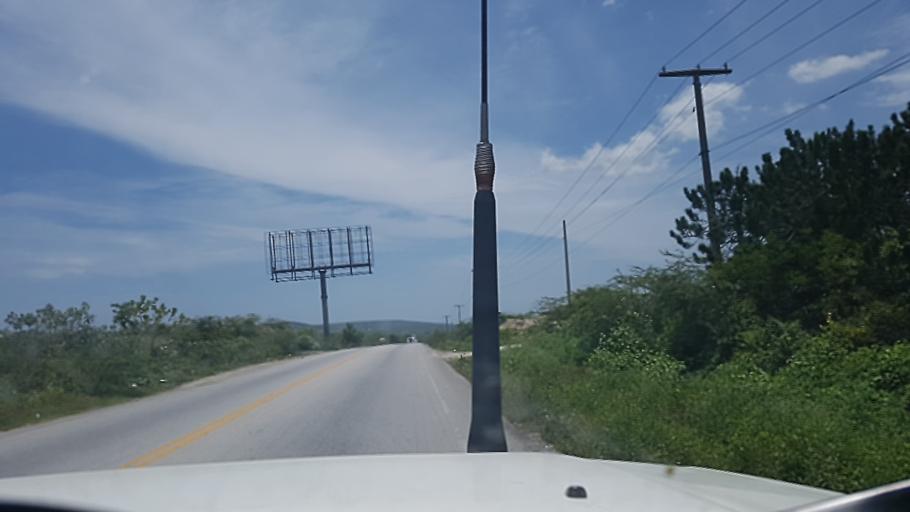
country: HT
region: Artibonite
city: Saint-Marc
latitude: 19.1521
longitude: -72.6336
